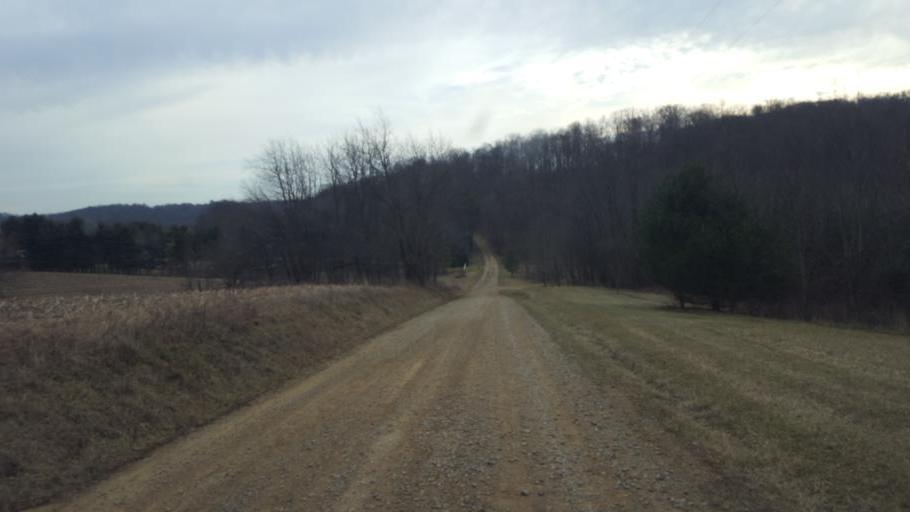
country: US
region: Ohio
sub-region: Knox County
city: Danville
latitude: 40.5341
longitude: -82.3317
